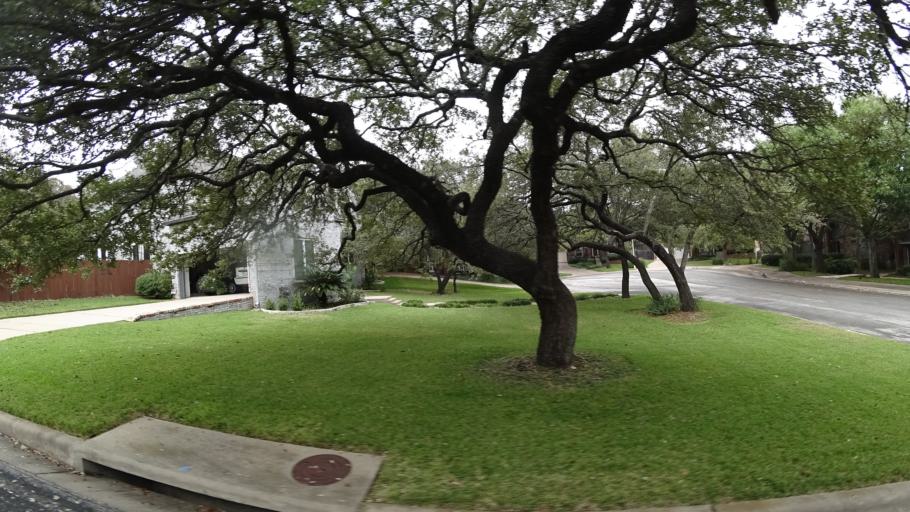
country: US
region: Texas
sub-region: Williamson County
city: Anderson Mill
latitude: 30.4413
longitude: -97.8237
